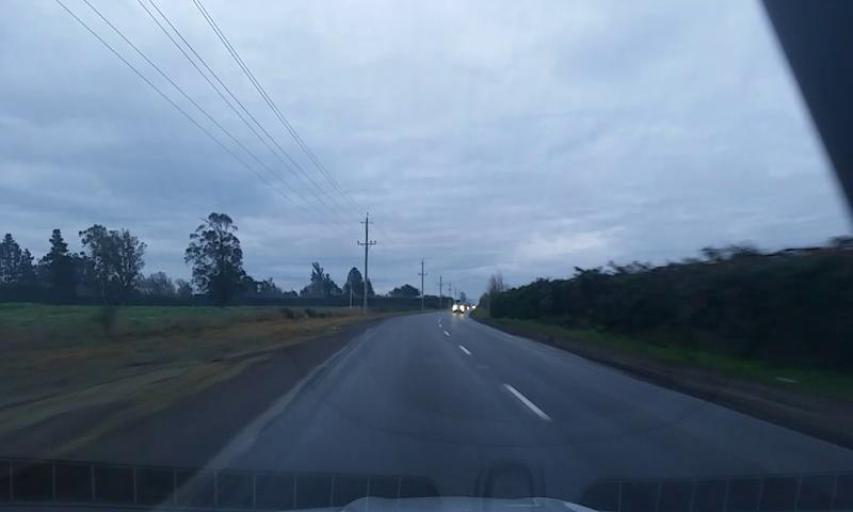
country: NZ
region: Canterbury
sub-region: Ashburton District
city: Rakaia
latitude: -43.7584
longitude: 171.9545
